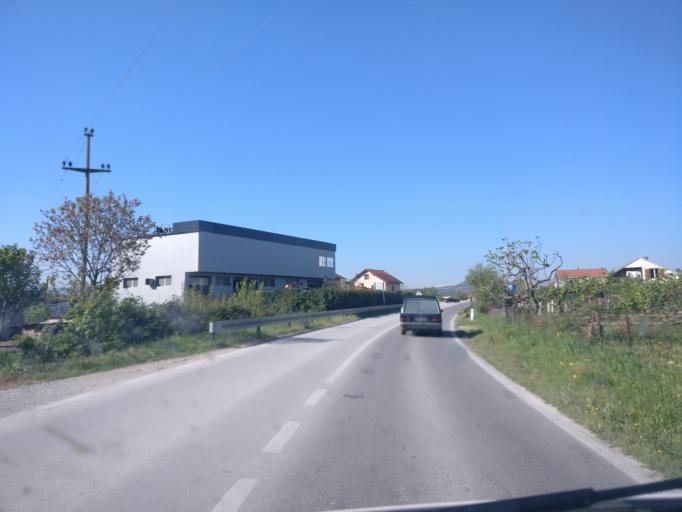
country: BA
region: Federation of Bosnia and Herzegovina
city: Tasovcici
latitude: 43.1098
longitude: 17.7218
